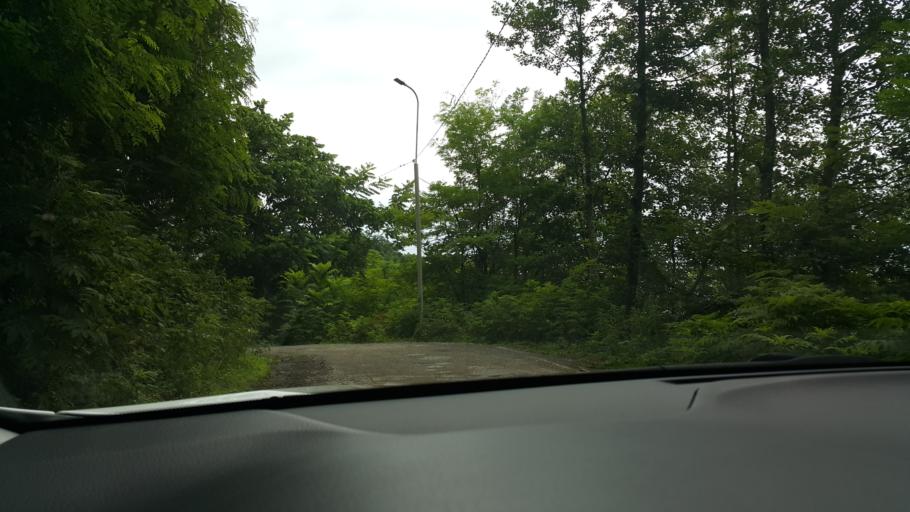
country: GE
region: Ajaria
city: Khelvachauri
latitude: 41.6132
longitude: 41.6556
